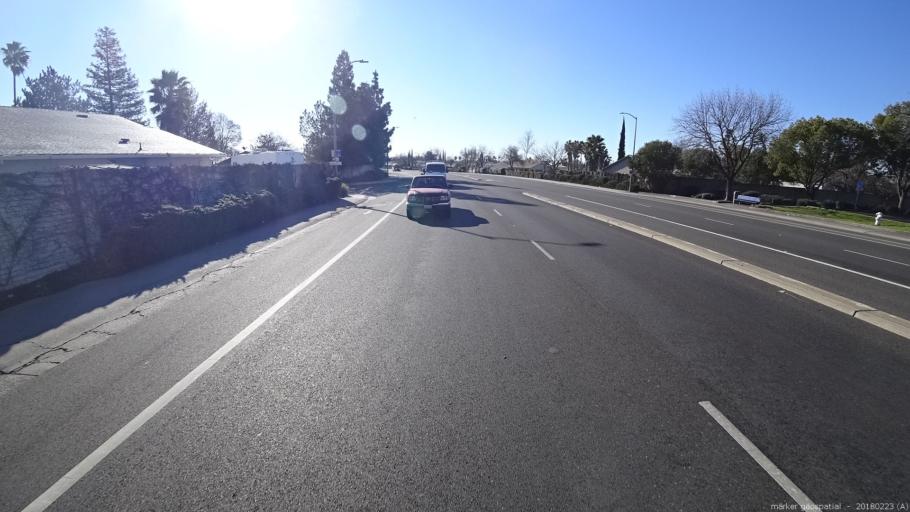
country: US
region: California
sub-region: Sacramento County
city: North Highlands
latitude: 38.7124
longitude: -121.3918
